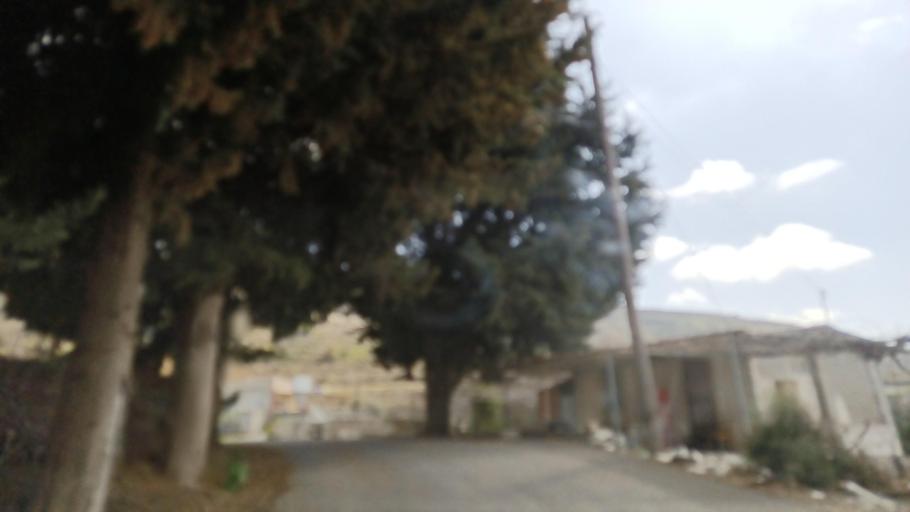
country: CY
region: Limassol
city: Pachna
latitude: 34.8586
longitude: 32.7534
